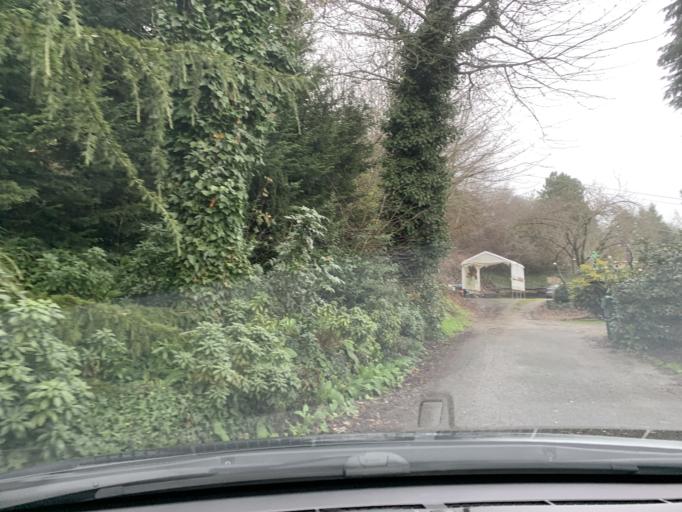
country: US
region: Washington
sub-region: King County
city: White Center
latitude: 47.5606
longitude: -122.3975
